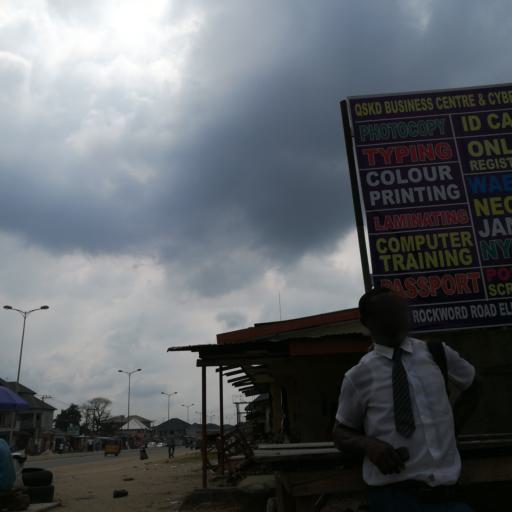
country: NG
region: Rivers
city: Port Harcourt
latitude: 4.8400
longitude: 7.0687
